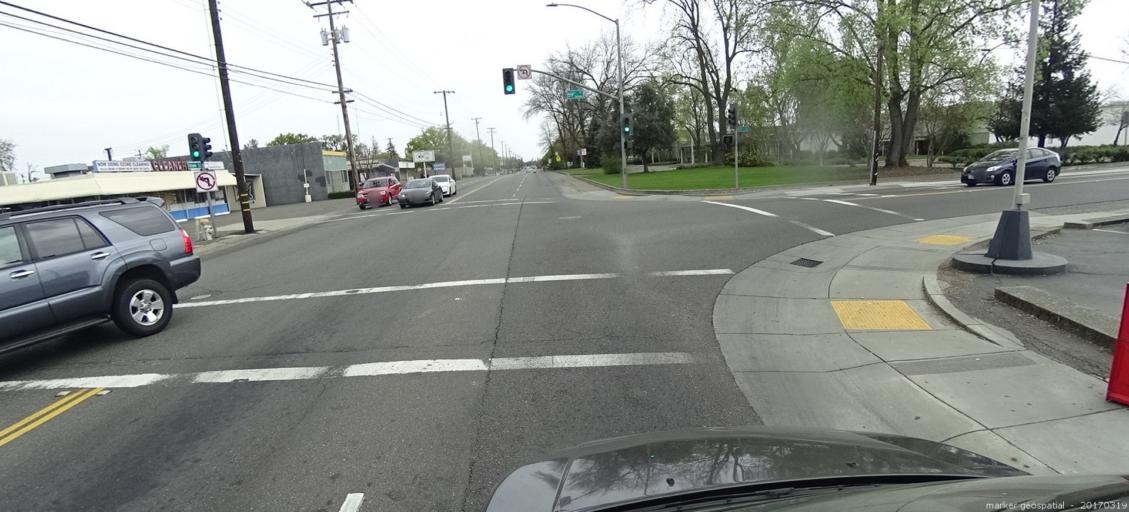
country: US
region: California
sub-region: Sacramento County
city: Sacramento
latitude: 38.5575
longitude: -121.4358
